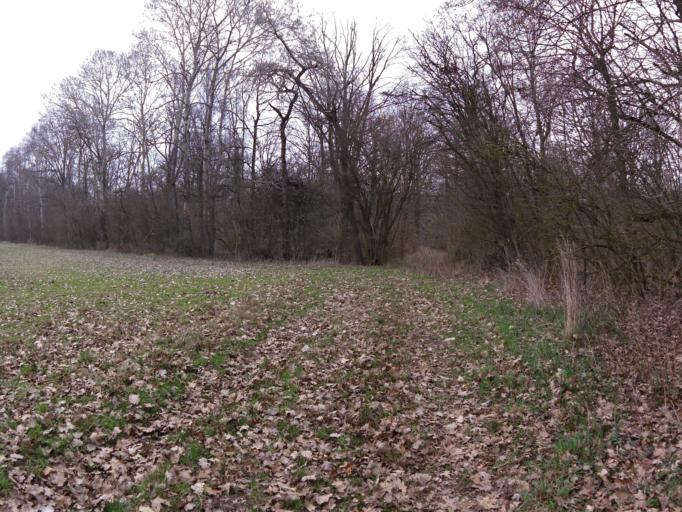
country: DE
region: Bavaria
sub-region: Regierungsbezirk Unterfranken
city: Rottendorf
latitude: 49.8173
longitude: 10.0391
